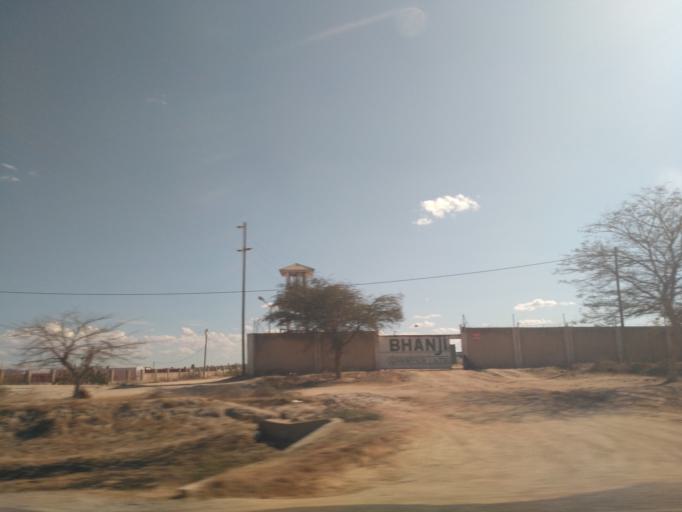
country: TZ
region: Dodoma
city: Dodoma
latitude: -6.1462
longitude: 35.7007
